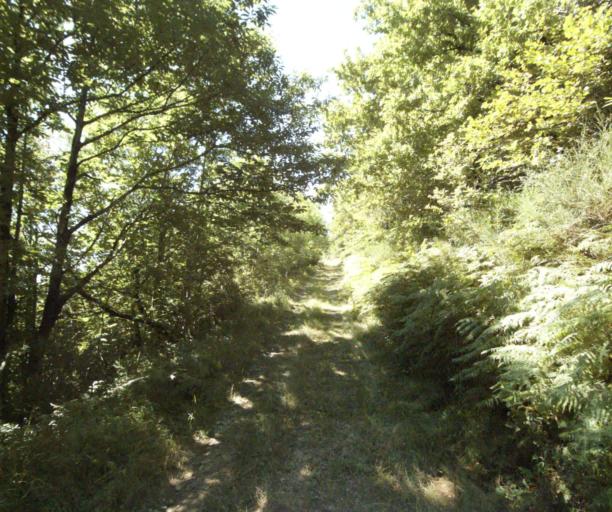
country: FR
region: Midi-Pyrenees
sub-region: Departement du Tarn
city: Soreze
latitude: 43.4394
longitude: 2.1021
